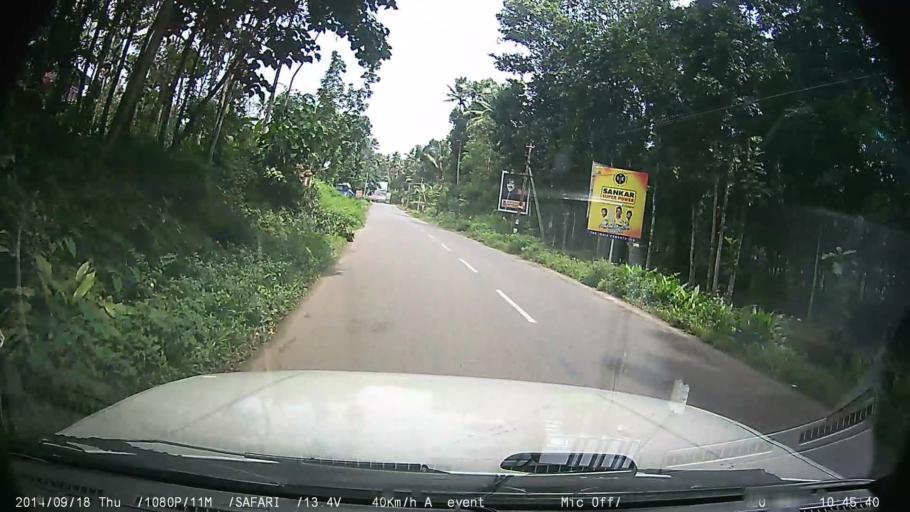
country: IN
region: Kerala
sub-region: Kottayam
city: Palackattumala
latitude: 9.7903
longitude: 76.5789
